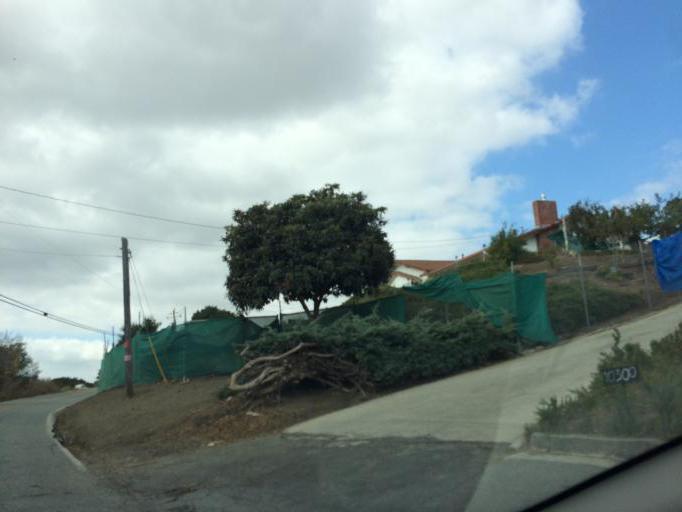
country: US
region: California
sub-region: Santa Clara County
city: East Foothills
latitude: 37.3782
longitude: -121.7951
